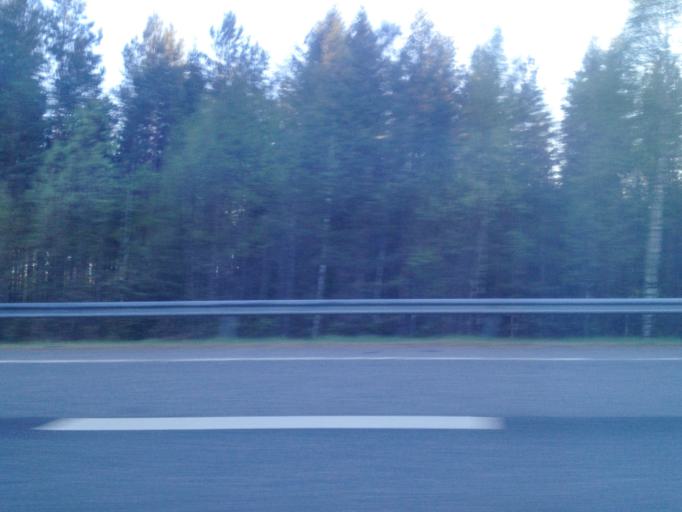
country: FI
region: Haeme
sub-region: Haemeenlinna
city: Haemeenlinna
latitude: 60.9345
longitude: 24.5165
